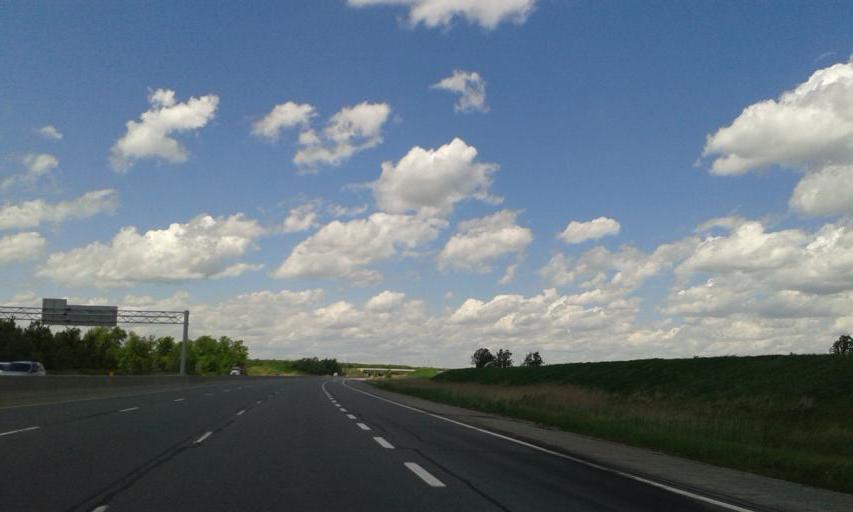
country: CA
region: Ontario
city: Burlington
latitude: 43.3909
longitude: -79.8339
